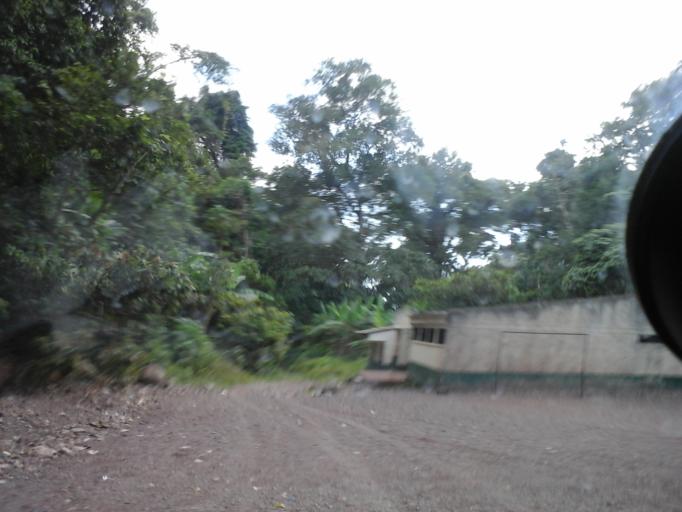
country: CO
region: Cesar
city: Manaure Balcon del Cesar
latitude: 10.2943
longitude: -73.0753
